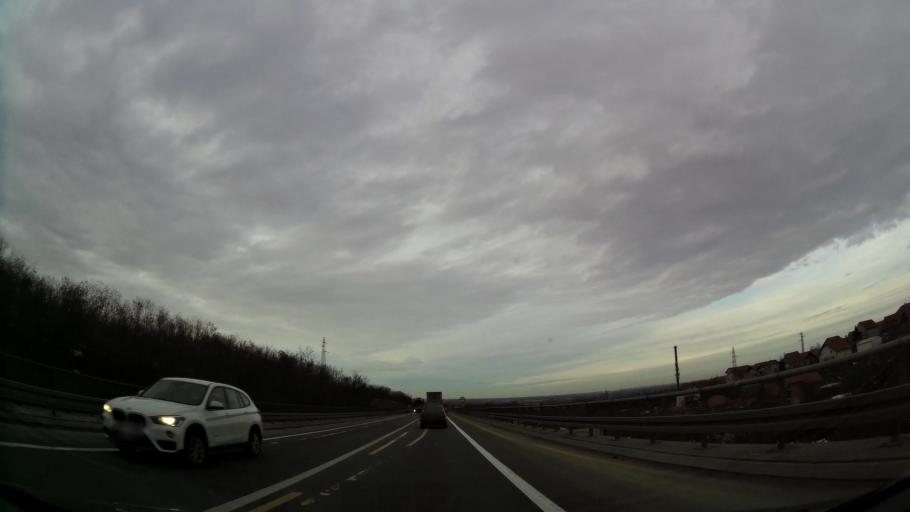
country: RS
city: Ostruznica
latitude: 44.7195
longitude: 20.3598
